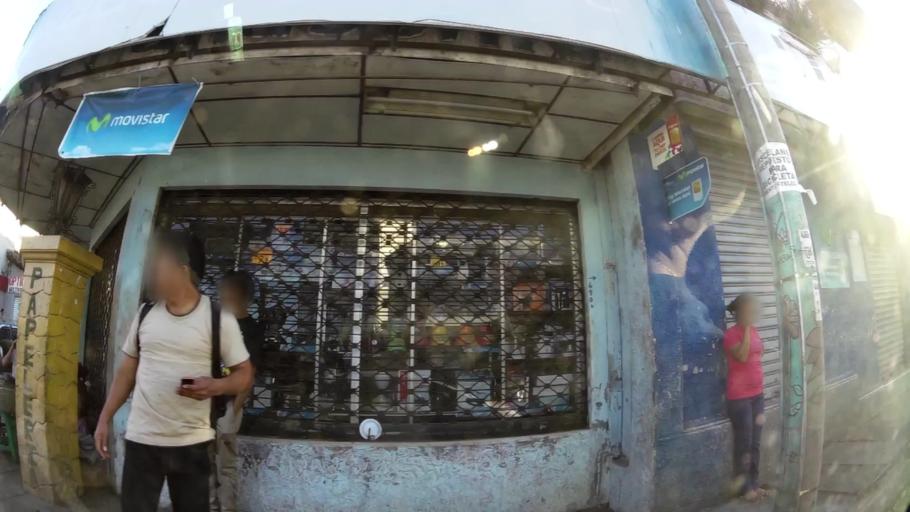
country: SV
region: Sonsonate
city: Sonsonate
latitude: 13.7213
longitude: -89.7291
